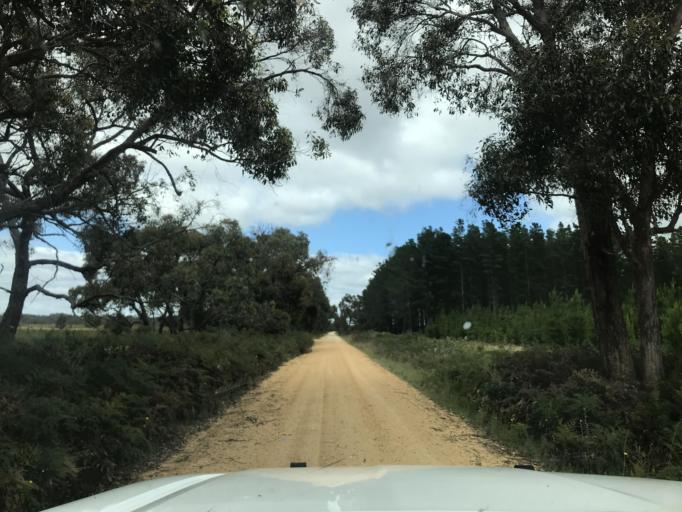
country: AU
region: South Australia
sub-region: Wattle Range
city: Penola
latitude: -37.3177
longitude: 141.1511
